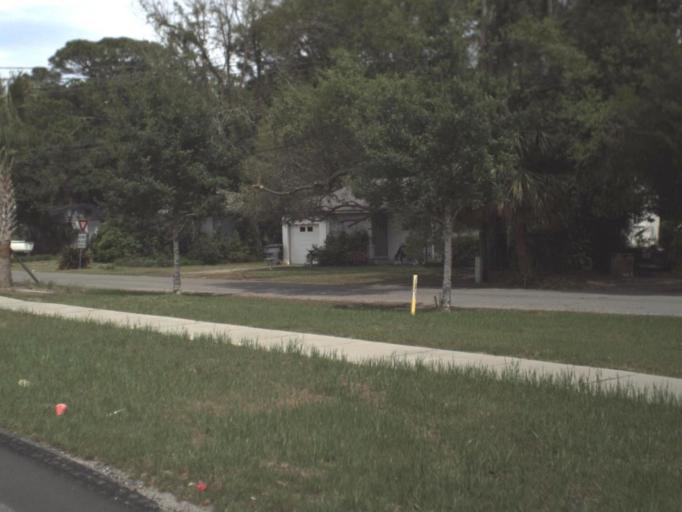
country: US
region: Florida
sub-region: Okaloosa County
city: Ocean City
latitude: 30.4291
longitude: -86.6062
